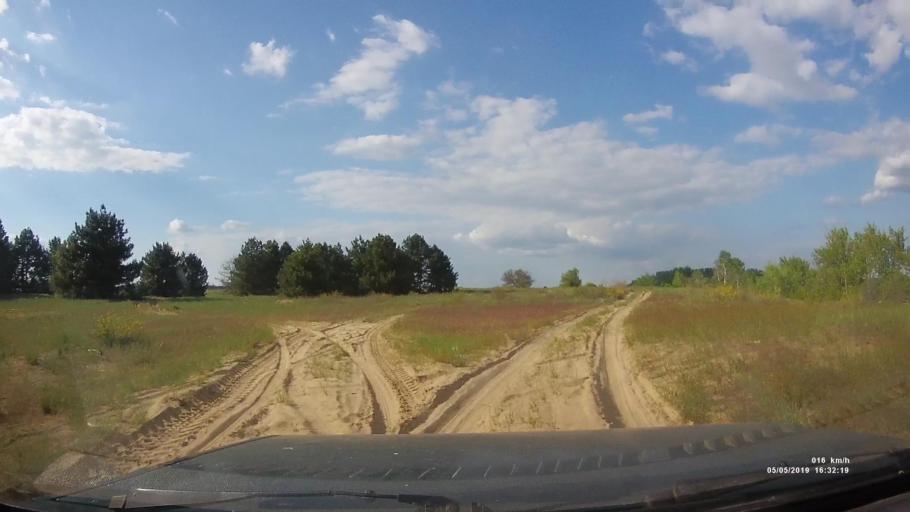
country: RU
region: Rostov
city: Ust'-Donetskiy
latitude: 47.7786
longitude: 41.0141
